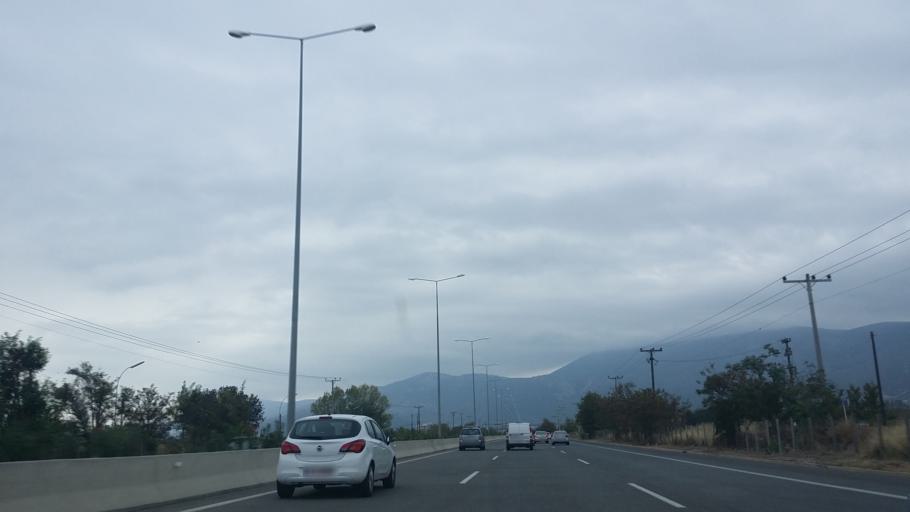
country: GR
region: Attica
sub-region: Nomarchia Anatolikis Attikis
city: Avlonas
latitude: 38.2797
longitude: 23.6864
